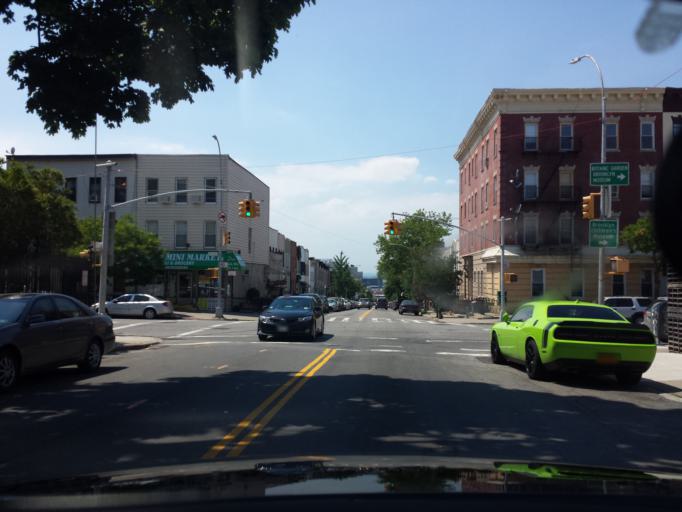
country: US
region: New York
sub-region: Kings County
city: Brooklyn
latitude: 40.6591
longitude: -73.9882
